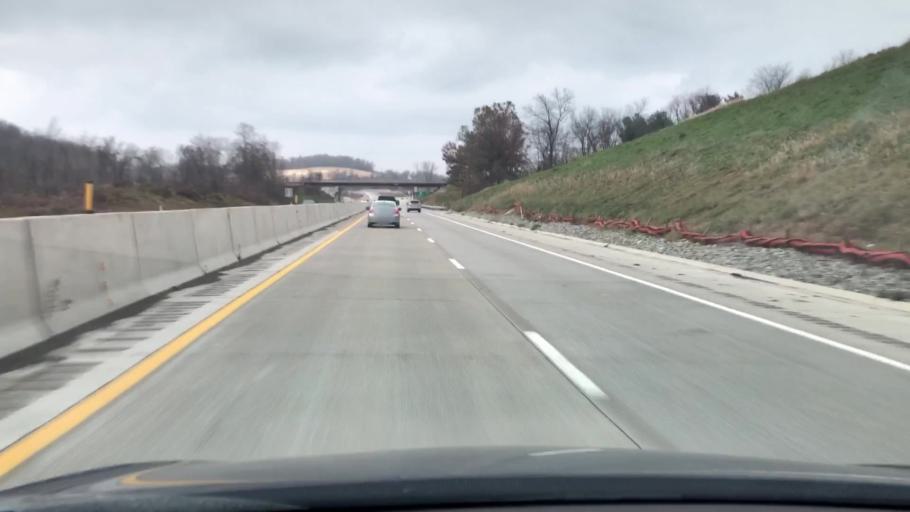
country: US
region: Pennsylvania
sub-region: Westmoreland County
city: Mount Pleasant
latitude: 40.1465
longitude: -79.5600
